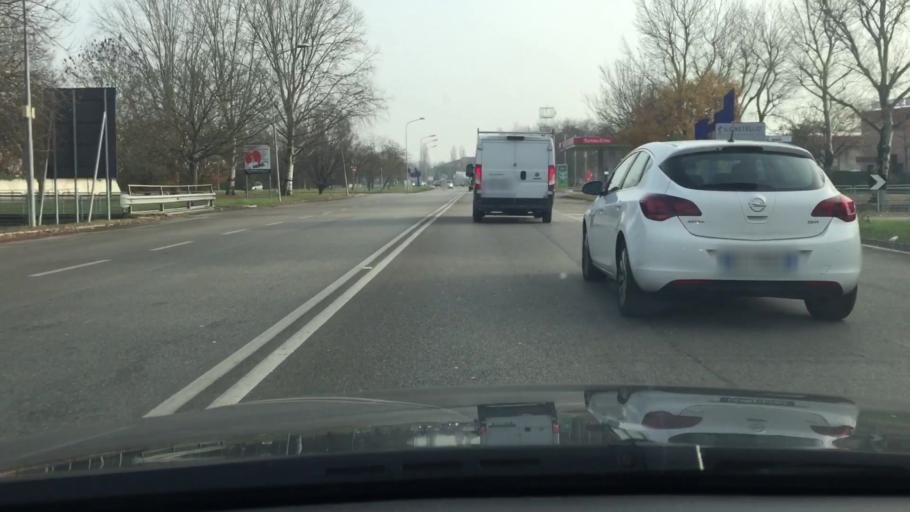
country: IT
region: Emilia-Romagna
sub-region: Provincia di Ferrara
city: Ferrara
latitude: 44.8177
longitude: 11.6068
